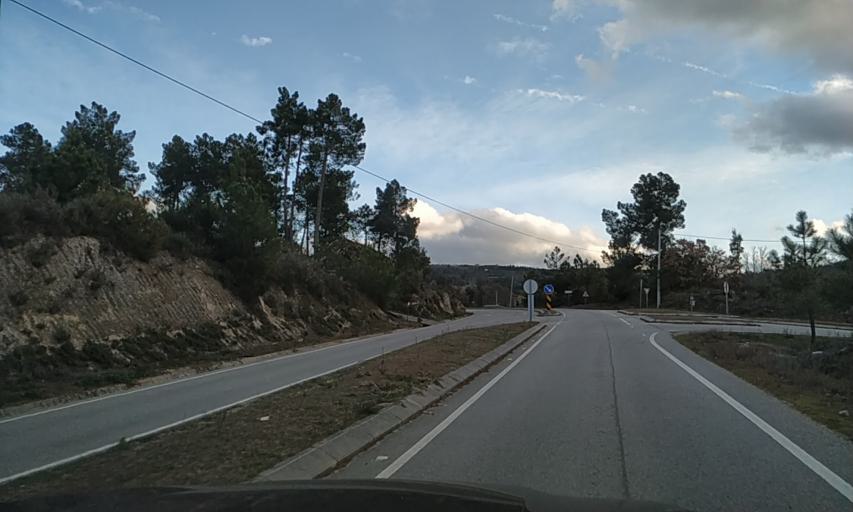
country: PT
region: Braganca
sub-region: Carrazeda de Ansiaes
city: Carrazeda de Anciaes
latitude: 41.2636
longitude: -7.3249
